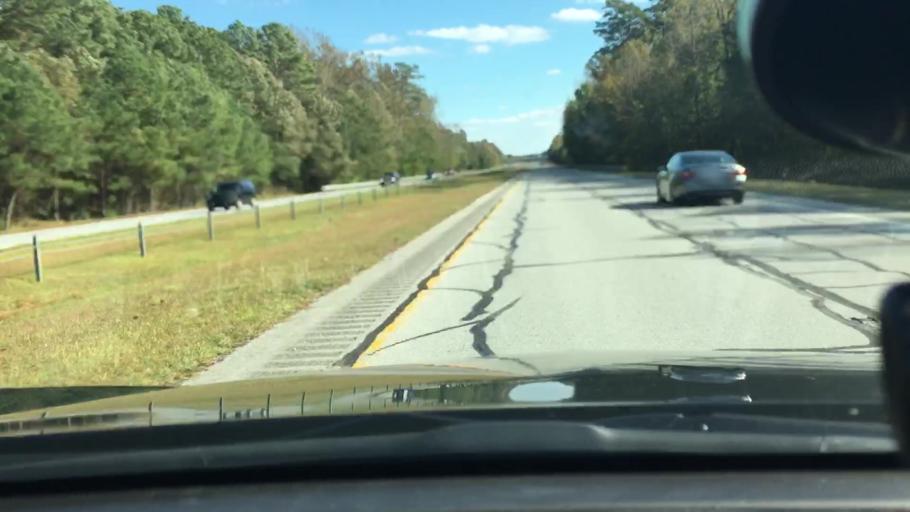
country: US
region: North Carolina
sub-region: Pitt County
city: Farmville
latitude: 35.6134
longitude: -77.5813
